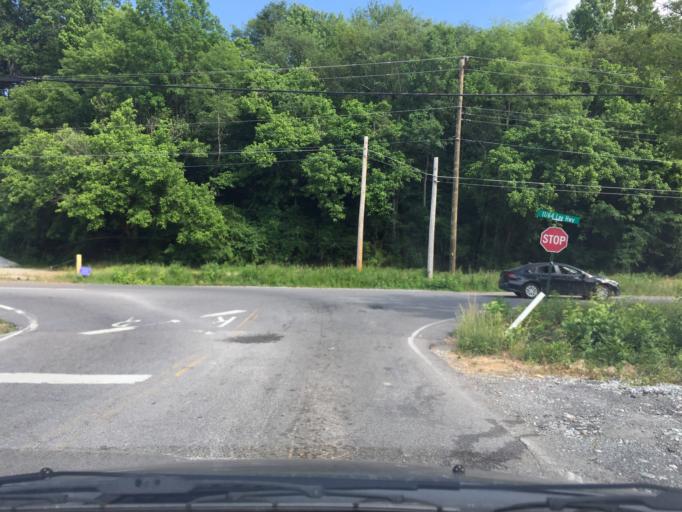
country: US
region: Tennessee
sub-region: Hamilton County
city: Collegedale
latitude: 35.0791
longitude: -85.0338
